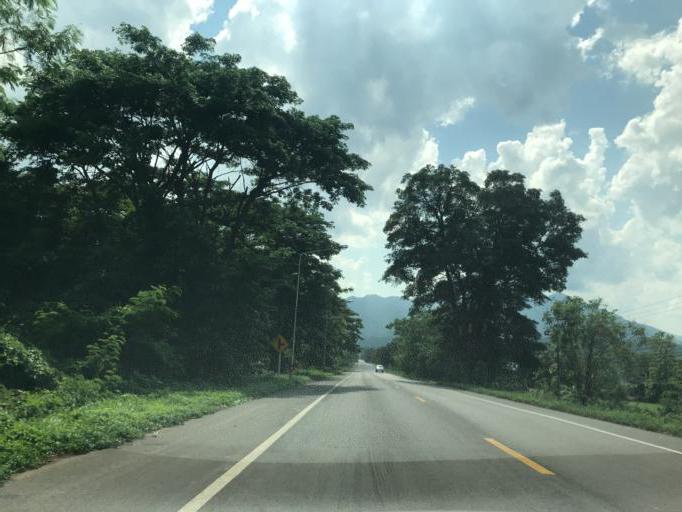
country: TH
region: Phayao
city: Phayao
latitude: 19.0904
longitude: 99.8385
